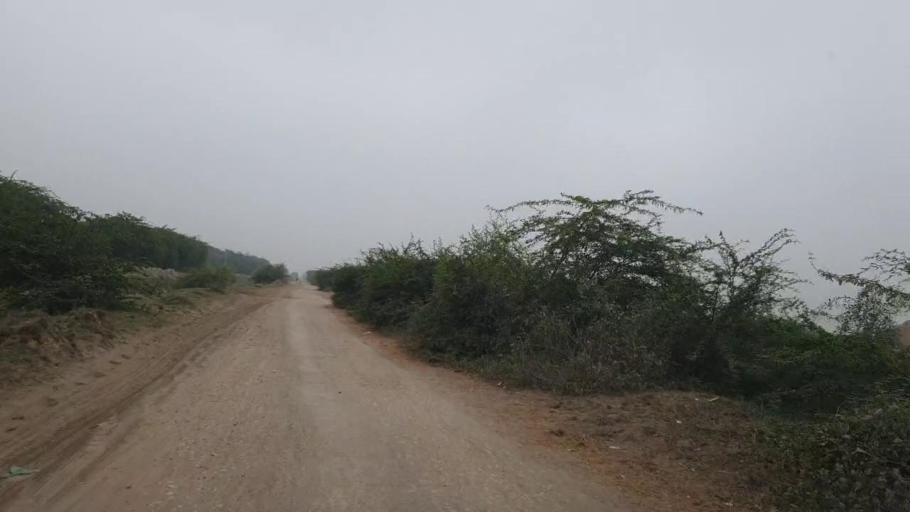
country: PK
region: Sindh
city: Badin
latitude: 24.6096
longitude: 68.6774
